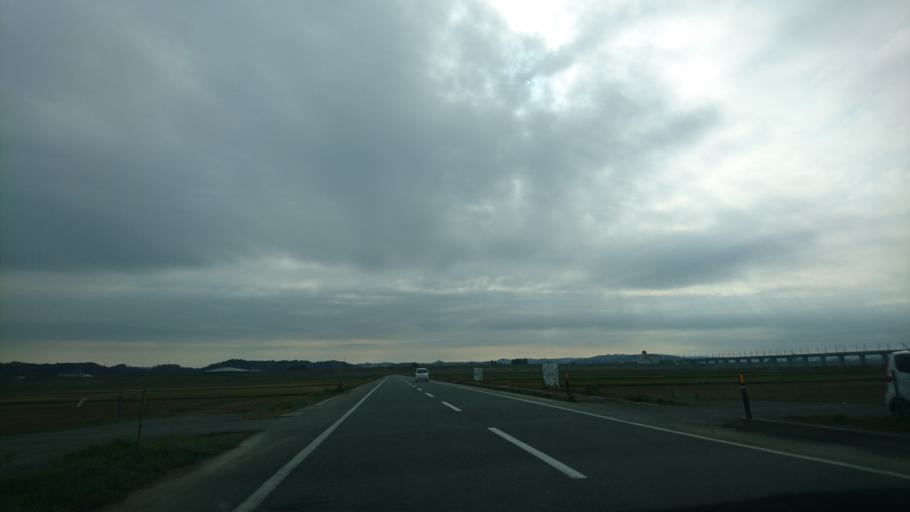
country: JP
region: Iwate
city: Ichinoseki
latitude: 38.9511
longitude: 141.1554
